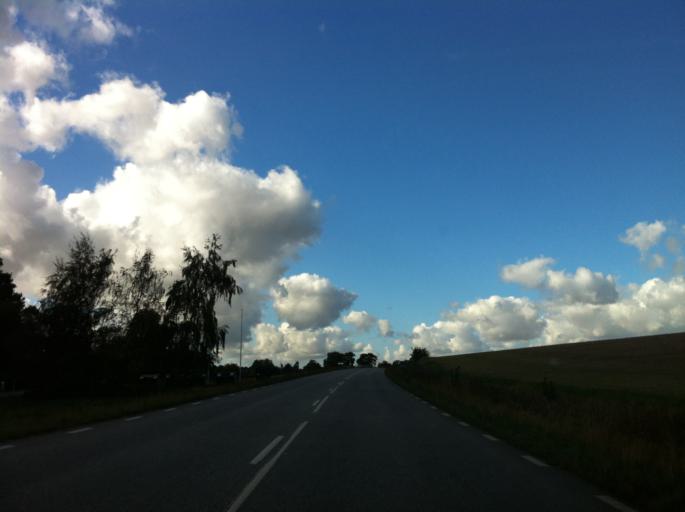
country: SE
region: Skane
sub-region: Eslovs Kommun
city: Eslov
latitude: 55.7611
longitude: 13.3285
